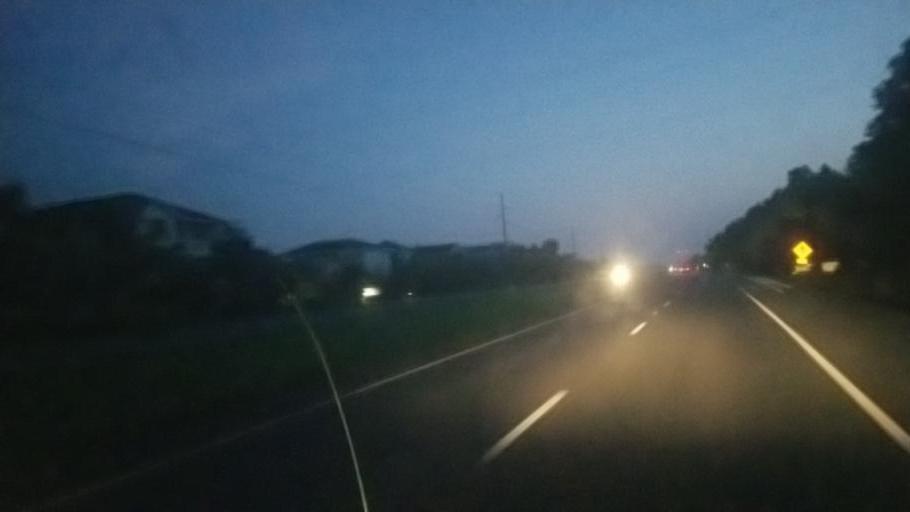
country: US
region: Delaware
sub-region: Sussex County
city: Bethany Beach
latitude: 38.5769
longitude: -75.0605
